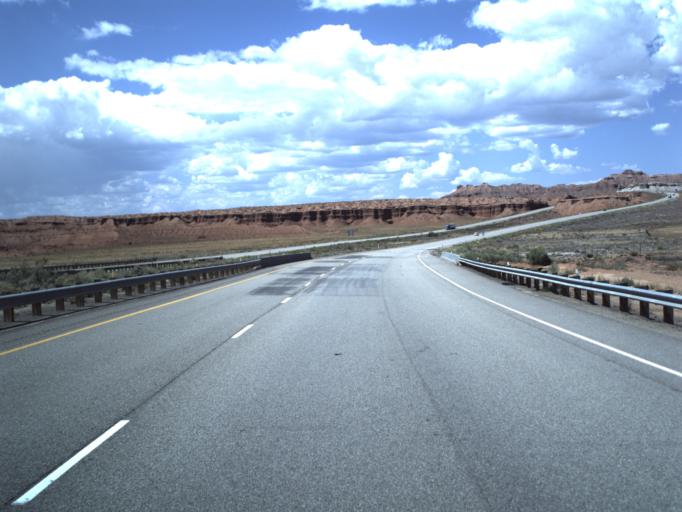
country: US
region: Utah
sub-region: Emery County
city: Ferron
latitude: 38.8396
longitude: -111.0713
